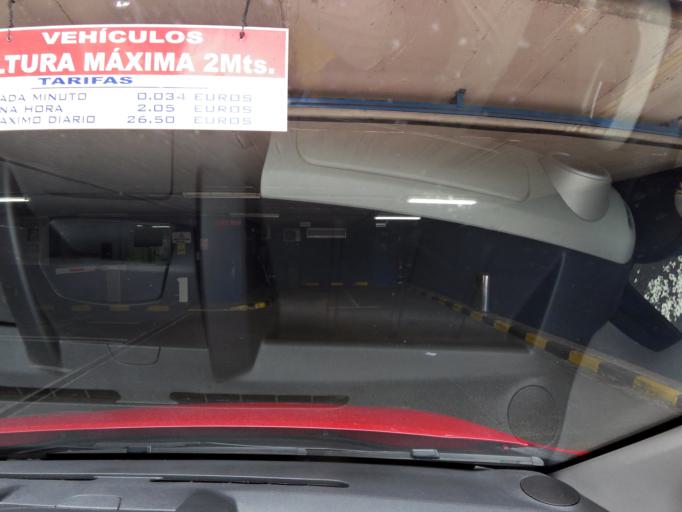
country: ES
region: Canary Islands
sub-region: Provincia de Las Palmas
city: Las Palmas de Gran Canaria
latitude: 28.1411
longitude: -15.4301
